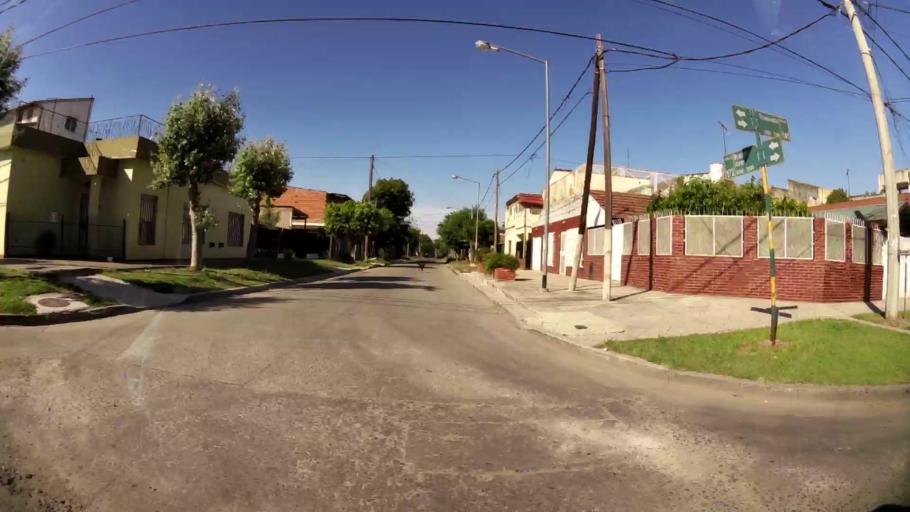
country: AR
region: Buenos Aires
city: Hurlingham
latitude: -34.5591
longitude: -58.6029
